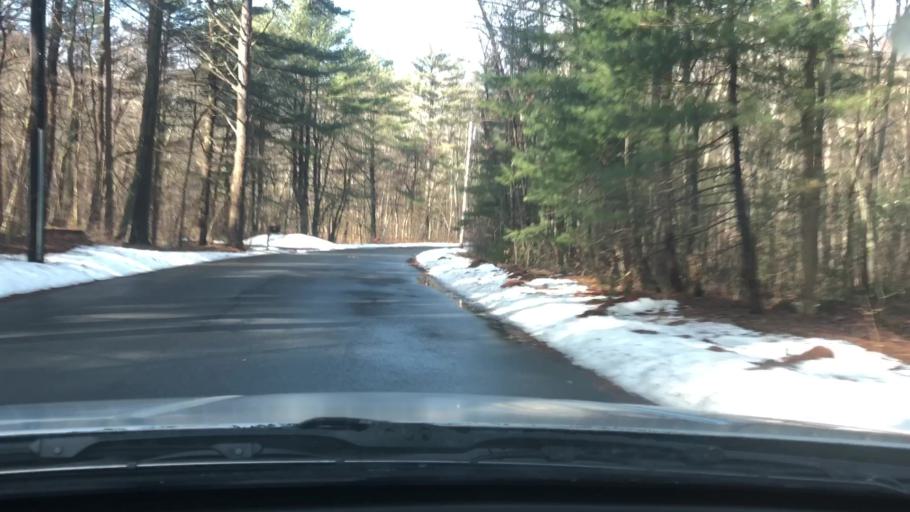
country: US
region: Massachusetts
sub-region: Middlesex County
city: West Concord
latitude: 42.4996
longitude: -71.3921
